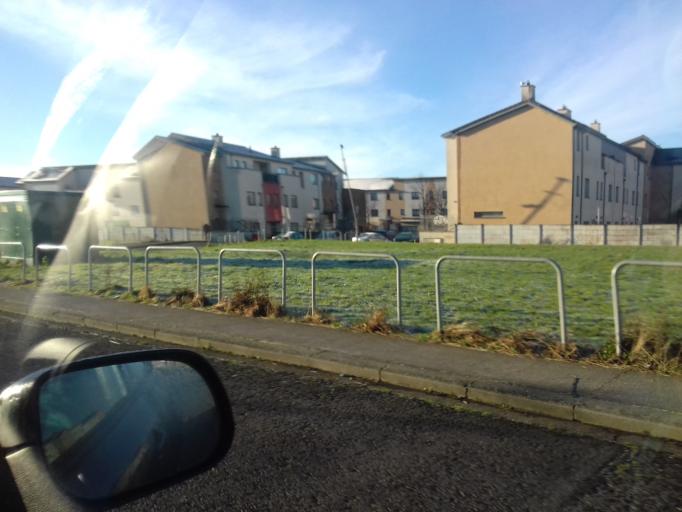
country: IE
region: Leinster
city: Ballymun
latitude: 53.3935
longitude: -6.2697
